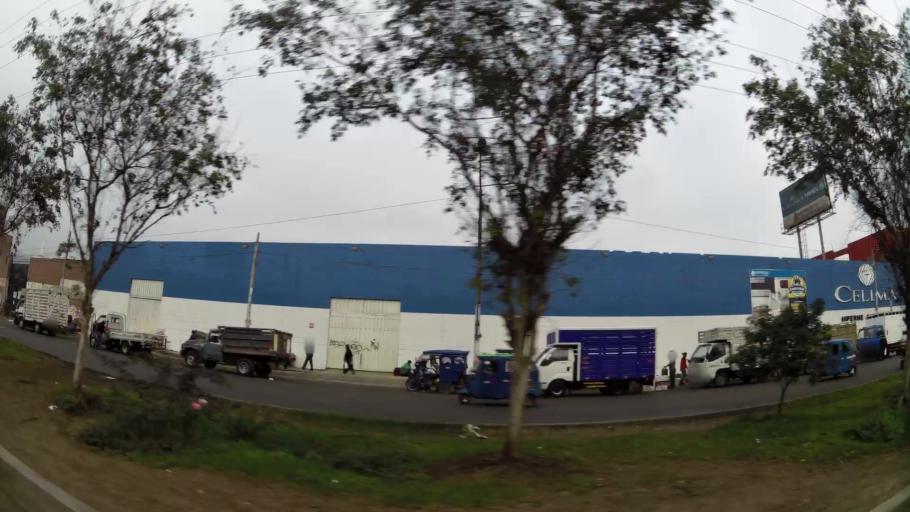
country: PE
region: Lima
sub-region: Lima
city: Independencia
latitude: -12.0052
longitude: -77.0048
